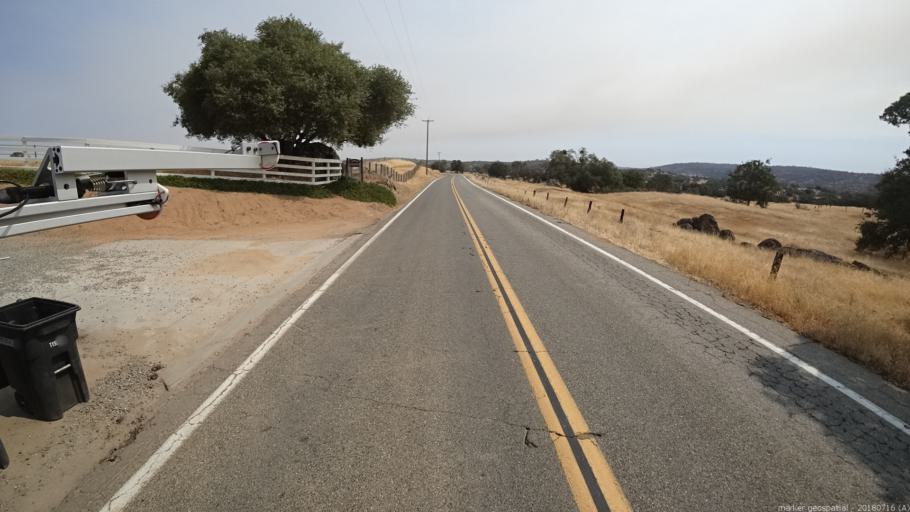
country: US
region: California
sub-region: Madera County
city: Yosemite Lakes
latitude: 37.1978
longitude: -119.9081
